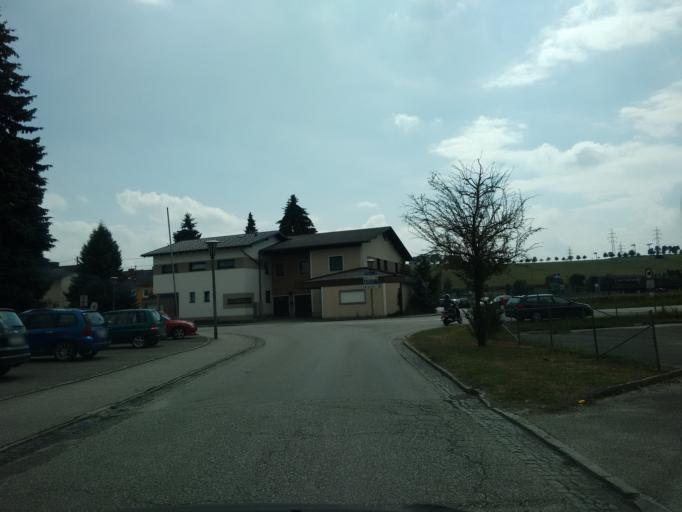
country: AT
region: Upper Austria
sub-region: Politischer Bezirk Grieskirchen
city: Grieskirchen
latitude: 48.2357
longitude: 13.8210
